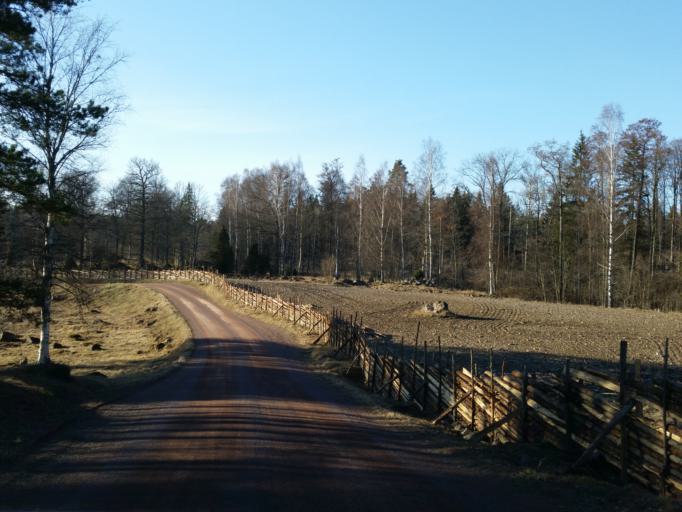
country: SE
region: Kalmar
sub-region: Oskarshamns Kommun
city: Oskarshamn
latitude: 57.3383
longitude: 16.4738
